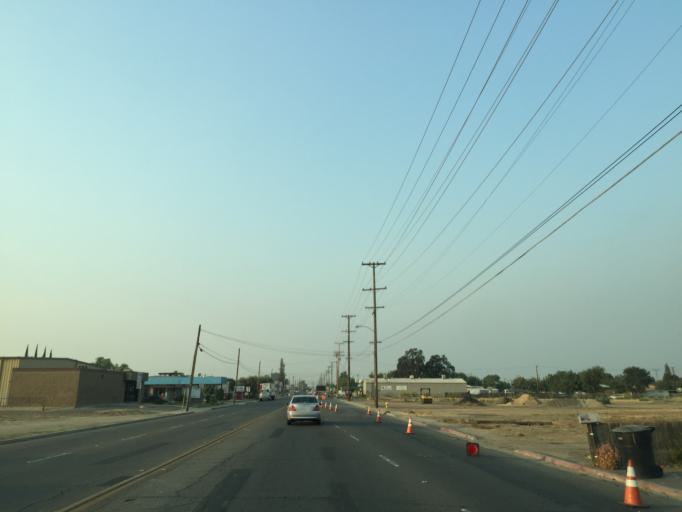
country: US
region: California
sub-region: Tulare County
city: Visalia
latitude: 36.3408
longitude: -119.2788
